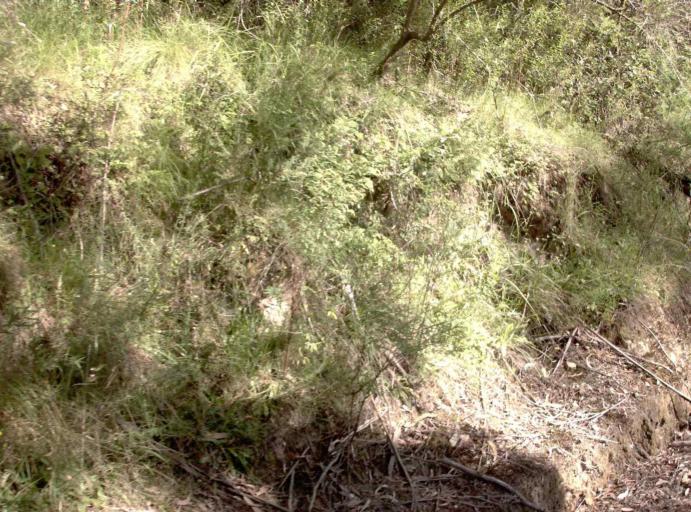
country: AU
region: Victoria
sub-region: East Gippsland
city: Lakes Entrance
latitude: -37.5040
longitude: 148.5419
